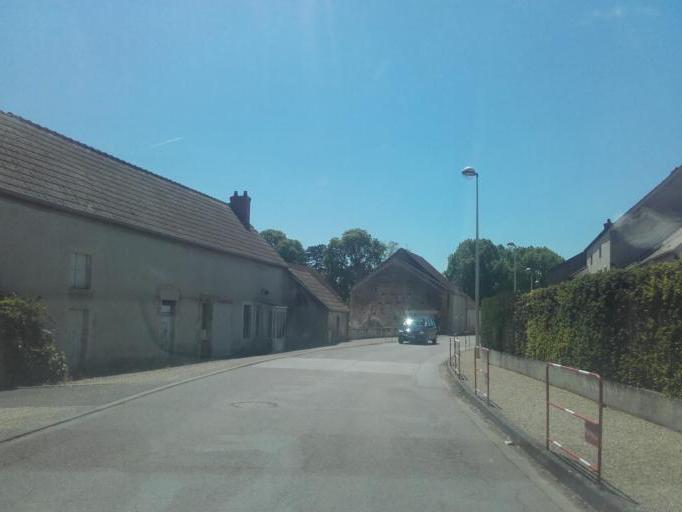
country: FR
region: Bourgogne
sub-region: Departement de la Cote-d'Or
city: Beaune
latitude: 47.0245
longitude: 4.8838
